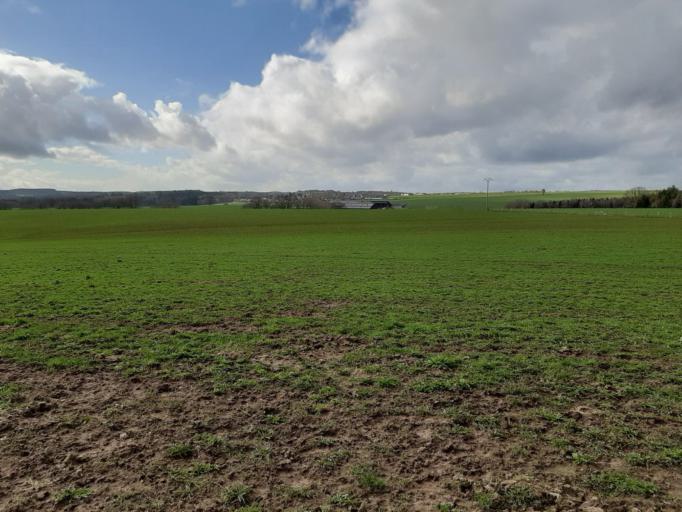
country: LU
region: Grevenmacher
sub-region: Canton d'Echternach
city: Beaufort
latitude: 49.8297
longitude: 6.3194
